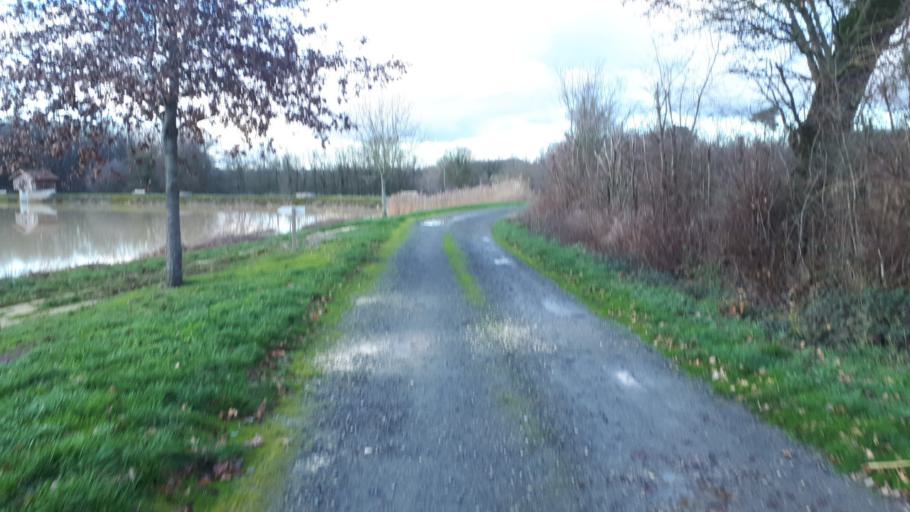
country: FR
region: Poitou-Charentes
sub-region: Departement de la Vienne
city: Pleumartin
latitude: 46.6371
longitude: 0.7640
